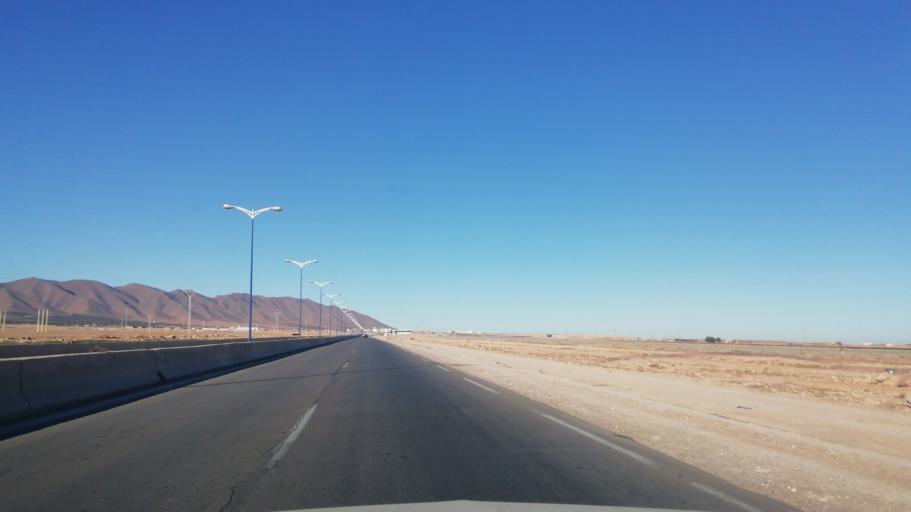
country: DZ
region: Wilaya de Naama
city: Naama
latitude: 33.4967
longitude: -0.2886
